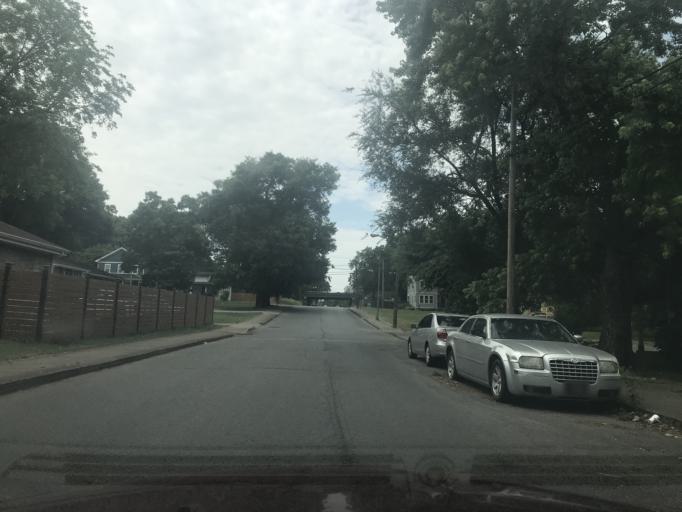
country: US
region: Tennessee
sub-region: Davidson County
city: Nashville
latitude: 36.1719
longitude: -86.8102
